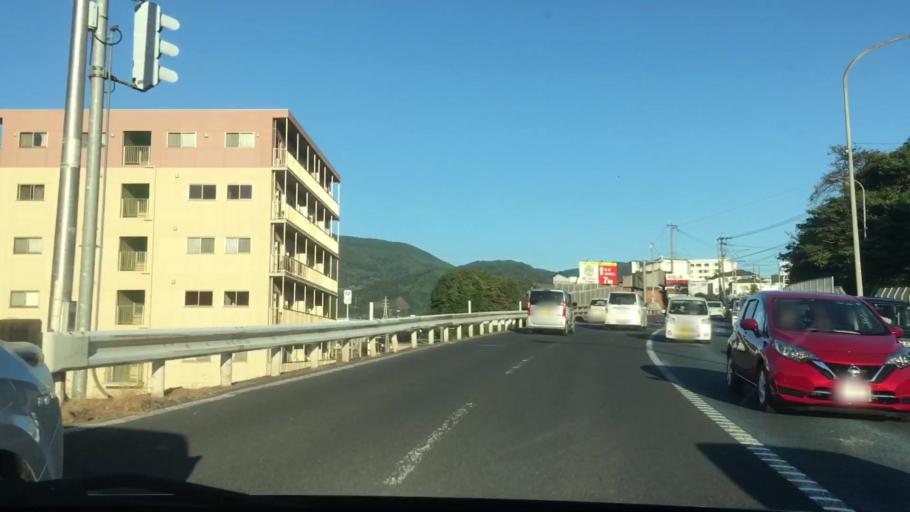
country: JP
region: Nagasaki
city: Sasebo
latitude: 33.1589
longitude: 129.7601
